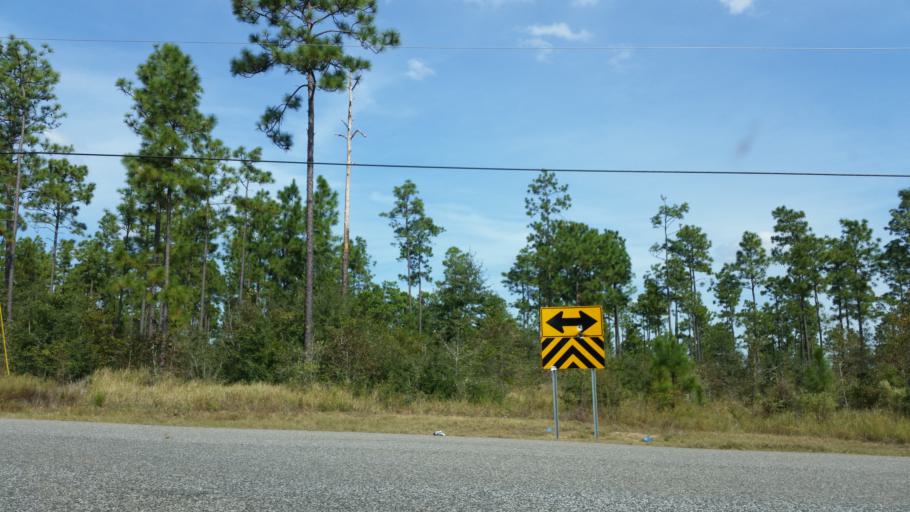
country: US
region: Alabama
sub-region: Baldwin County
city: Spanish Fort
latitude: 30.7328
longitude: -87.8358
